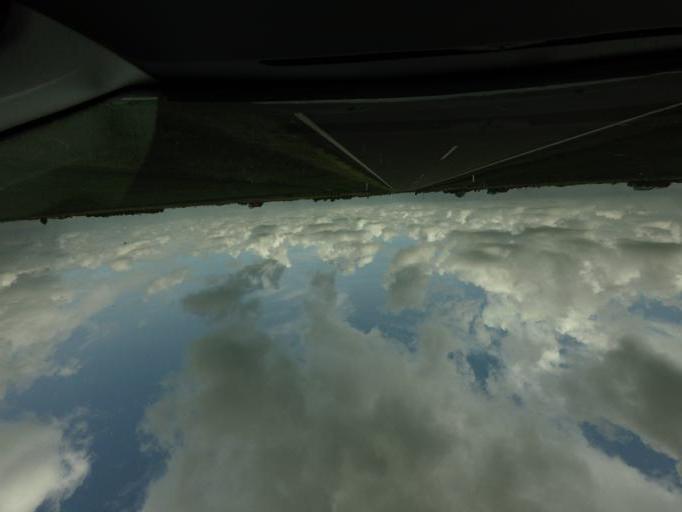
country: NL
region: Friesland
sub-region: Sudwest Fryslan
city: Workum
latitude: 53.0024
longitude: 5.4689
